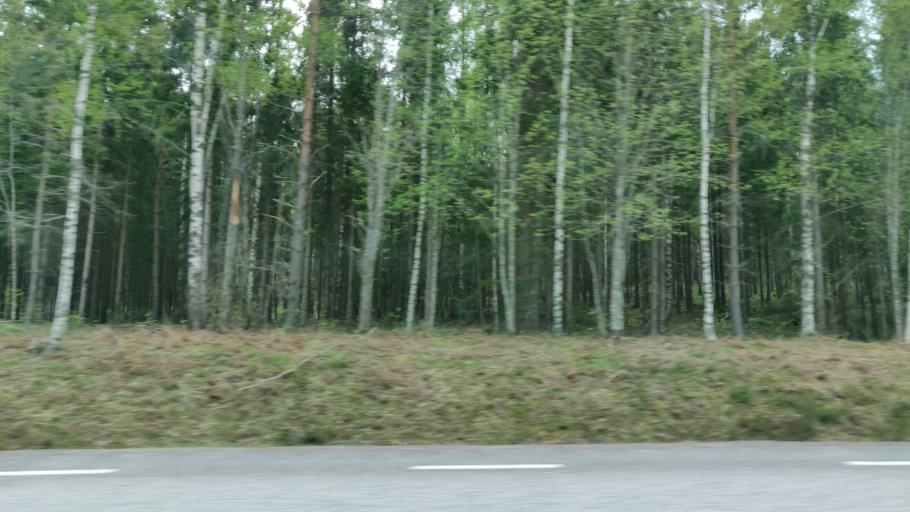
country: SE
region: Vaermland
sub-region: Forshaga Kommun
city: Deje
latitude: 59.6056
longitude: 13.4471
